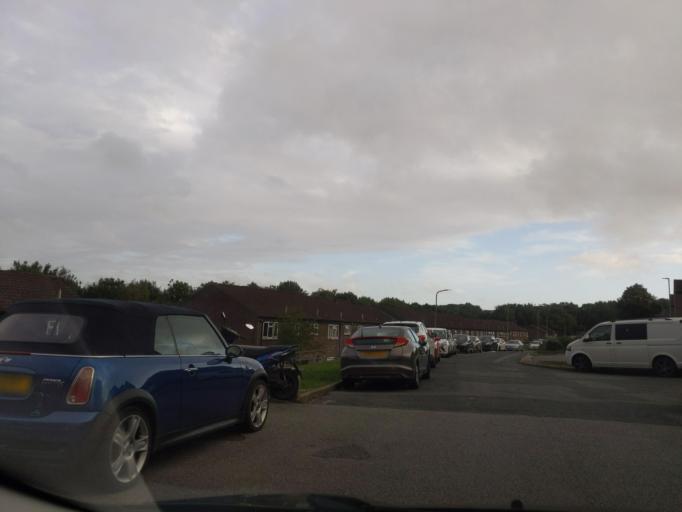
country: GB
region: England
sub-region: Devon
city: Plympton
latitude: 50.4055
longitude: -4.0907
